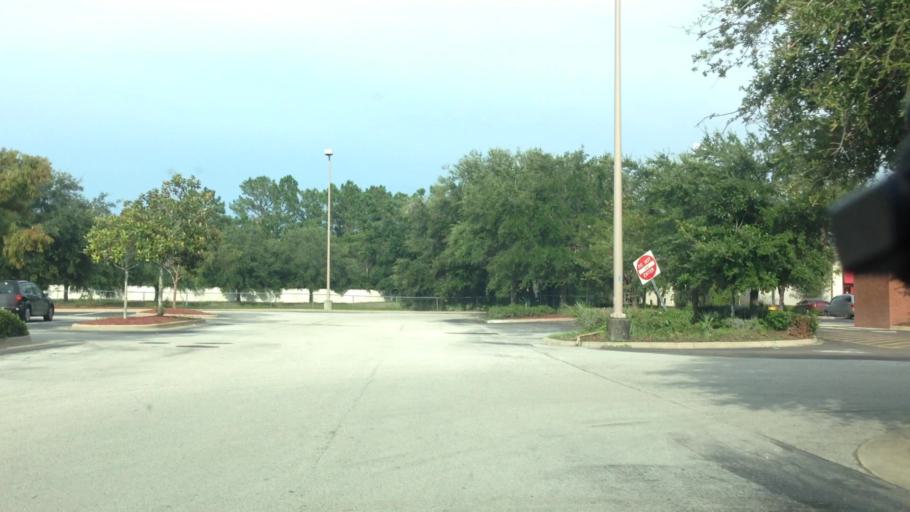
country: US
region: Florida
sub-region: Duval County
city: Atlantic Beach
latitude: 30.3207
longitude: -81.4675
